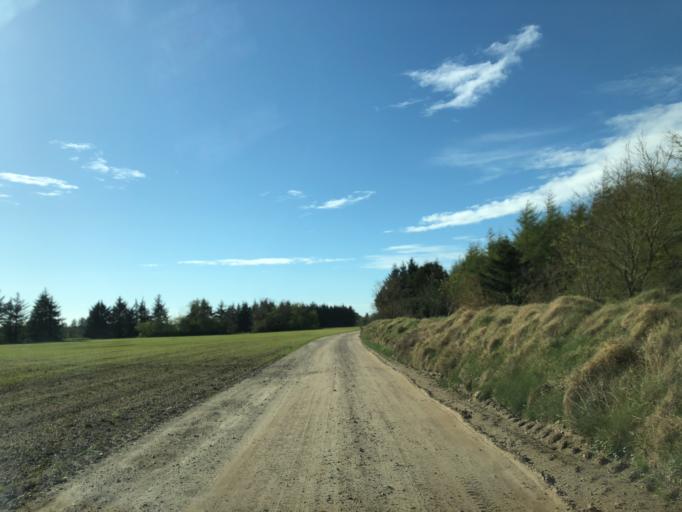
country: DK
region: Central Jutland
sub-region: Holstebro Kommune
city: Ulfborg
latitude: 56.2472
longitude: 8.3368
